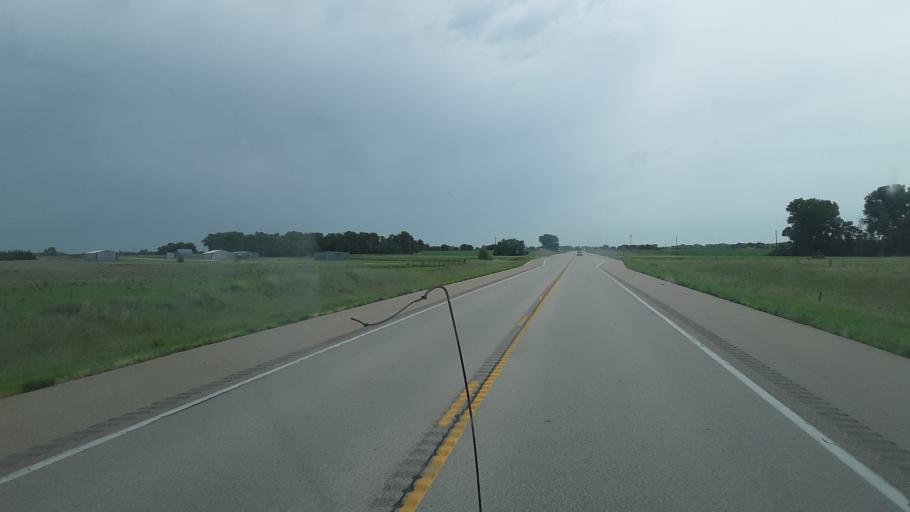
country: US
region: Kansas
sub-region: Stafford County
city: Stafford
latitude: 37.9729
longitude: -98.4013
